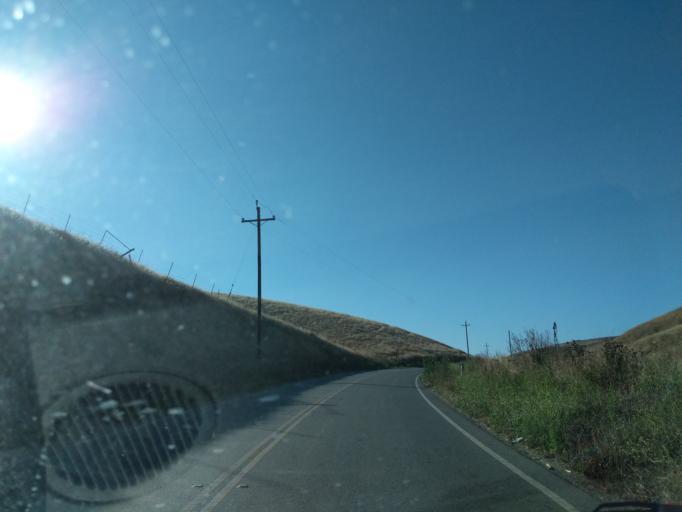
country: US
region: California
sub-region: San Benito County
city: Ridgemark
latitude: 36.8264
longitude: -121.3319
